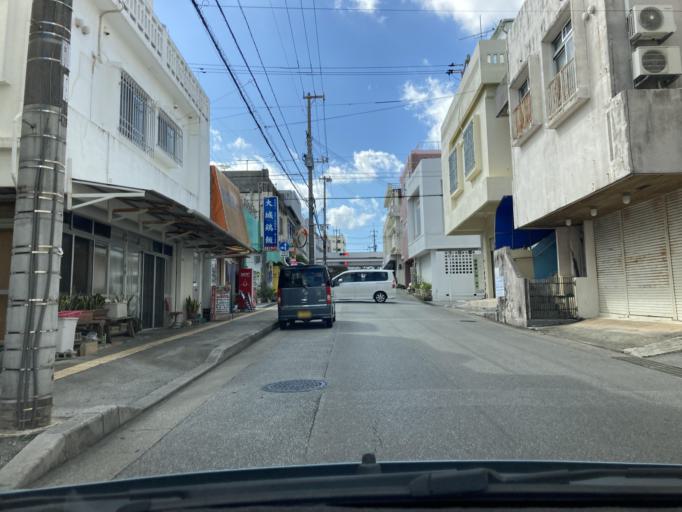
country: JP
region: Okinawa
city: Okinawa
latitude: 26.3395
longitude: 127.8010
